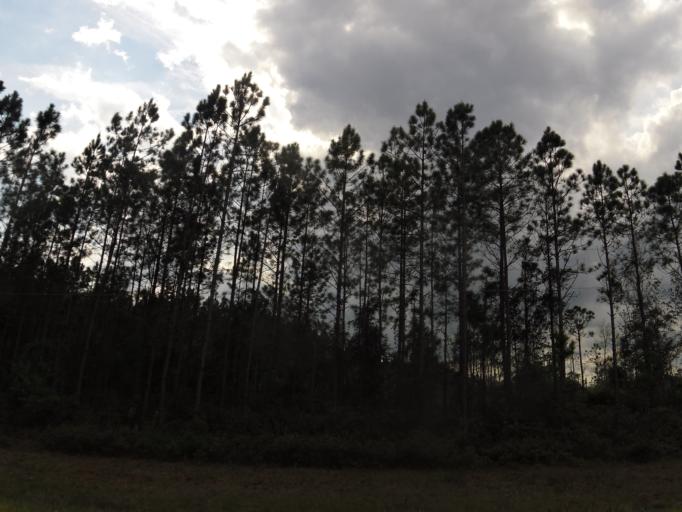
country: US
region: Georgia
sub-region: Charlton County
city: Folkston
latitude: 30.8689
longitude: -82.0144
